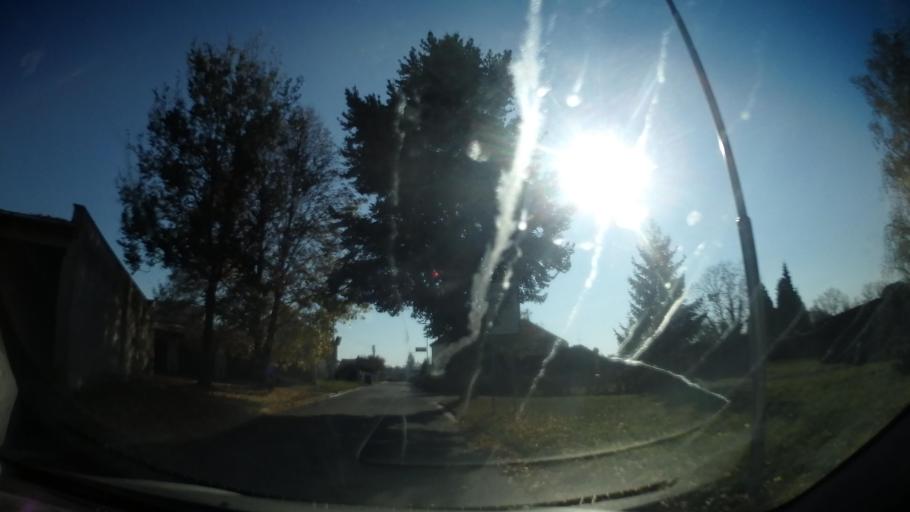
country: CZ
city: Tyniste nad Orlici
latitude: 50.1574
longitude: 16.0677
